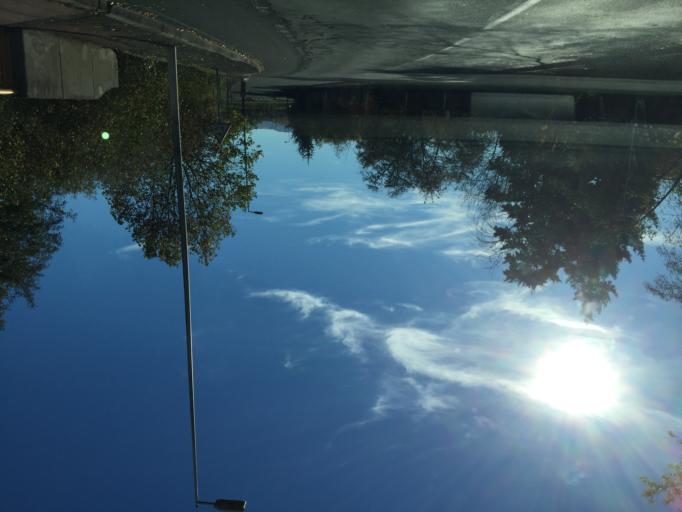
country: FR
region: Rhone-Alpes
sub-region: Departement de la Loire
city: Riorges
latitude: 46.0321
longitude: 4.0485
